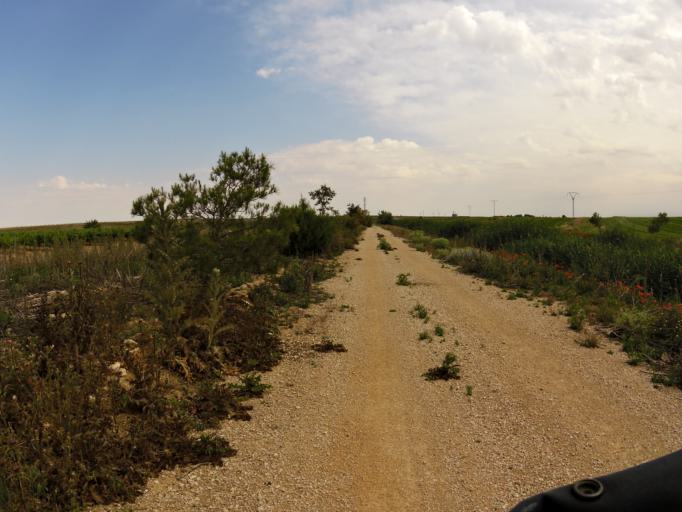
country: ES
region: Castille-La Mancha
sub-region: Provincia de Albacete
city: Valdeganga
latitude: 39.0547
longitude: -1.7557
